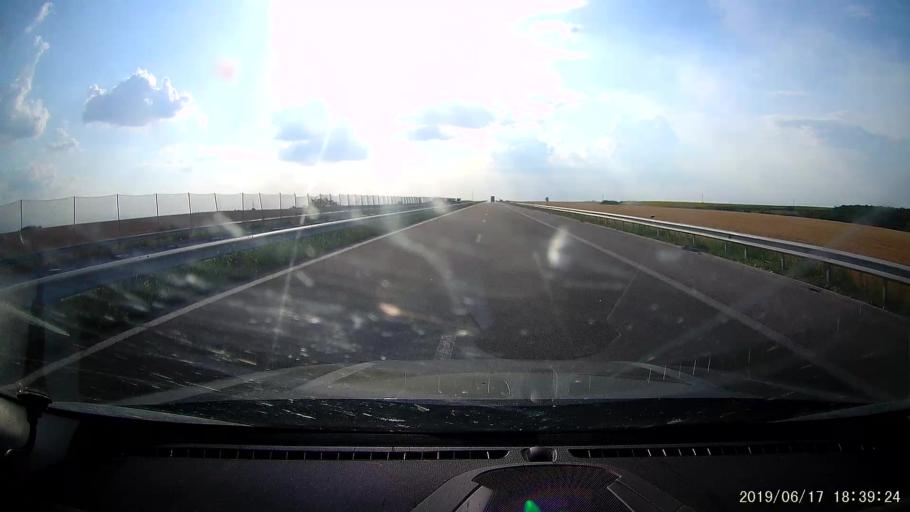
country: BG
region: Stara Zagora
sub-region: Obshtina Chirpan
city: Chirpan
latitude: 42.1448
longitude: 25.3084
